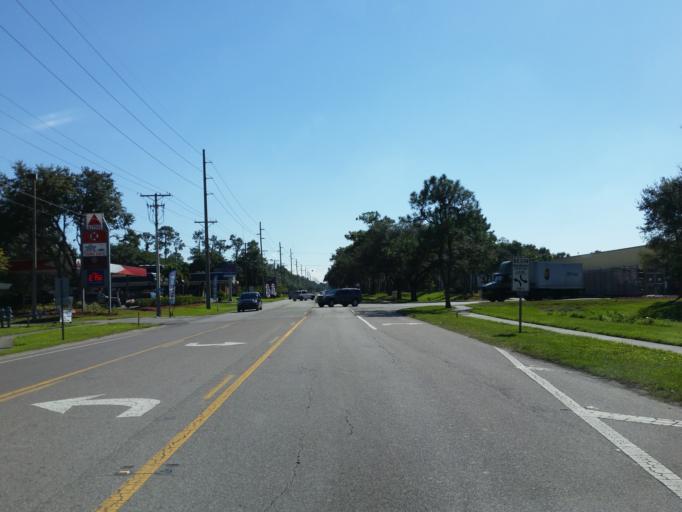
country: US
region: Florida
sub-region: Hillsborough County
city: Bloomingdale
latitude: 27.8919
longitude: -82.2693
